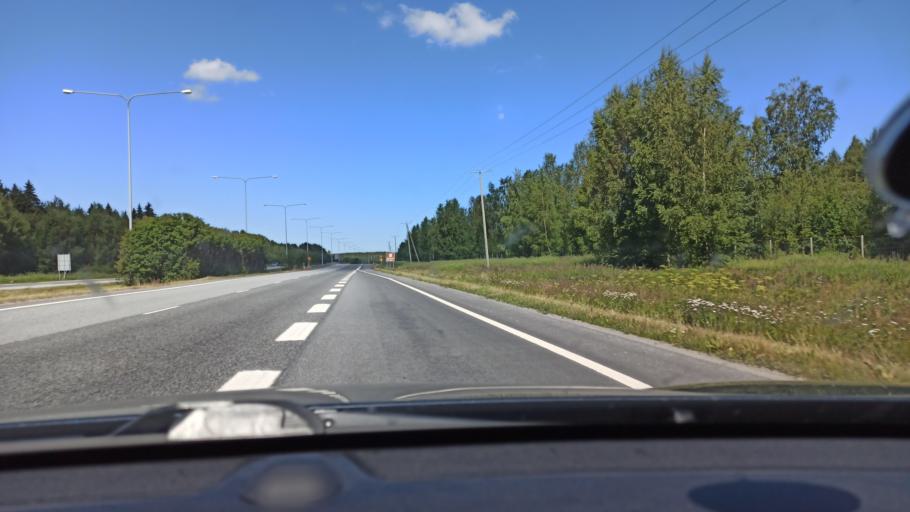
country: FI
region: Ostrobothnia
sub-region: Vaasa
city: Ristinummi
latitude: 63.0382
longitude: 21.7354
